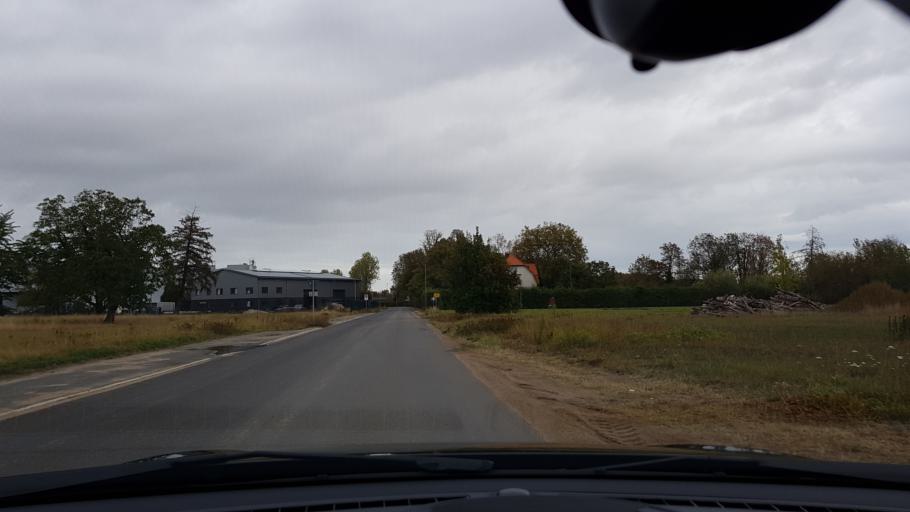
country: DE
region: North Rhine-Westphalia
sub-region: Regierungsbezirk Koln
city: Elsdorf
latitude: 50.9263
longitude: 6.5640
